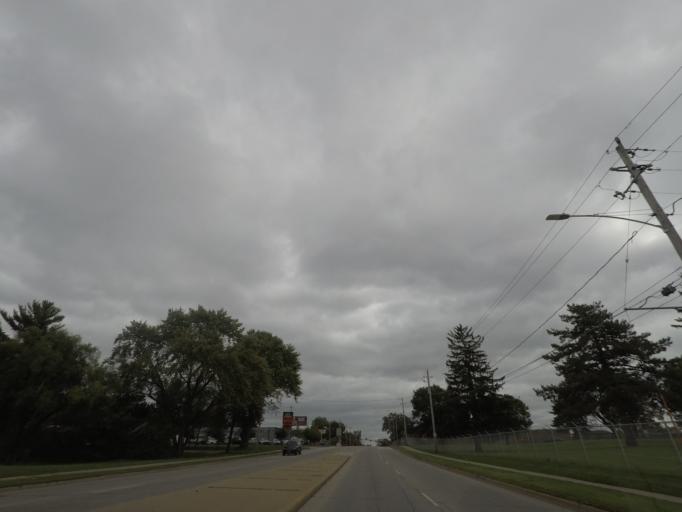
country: US
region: Iowa
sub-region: Polk County
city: Des Moines
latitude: 41.5264
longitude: -93.6149
